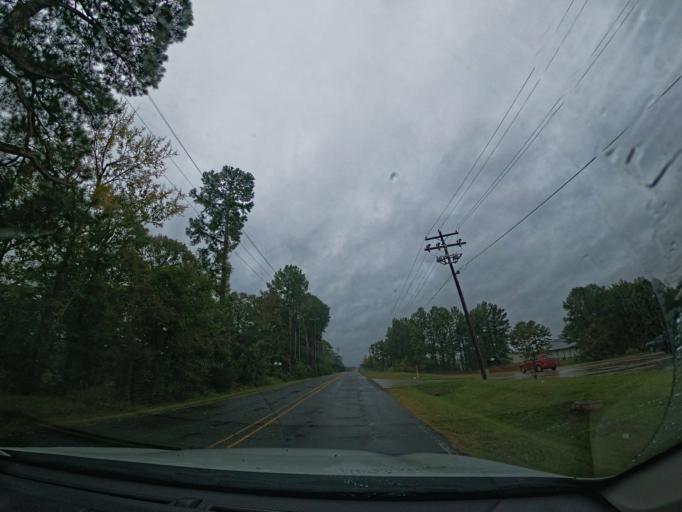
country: US
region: Louisiana
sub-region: Webster Parish
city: Minden
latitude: 32.6303
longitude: -93.2498
